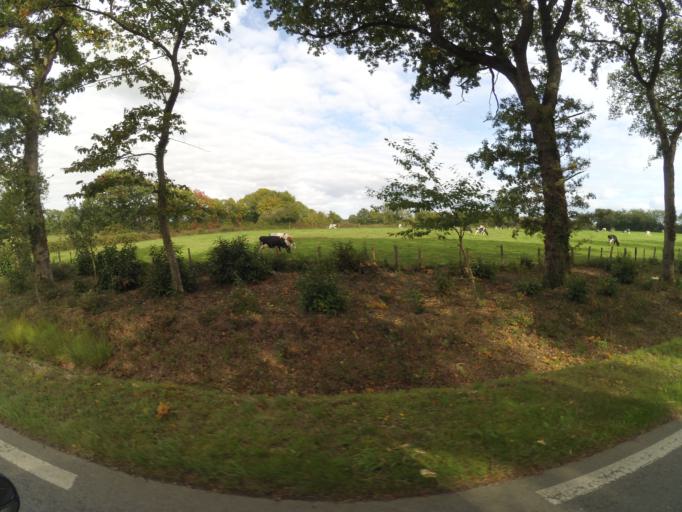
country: FR
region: Pays de la Loire
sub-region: Departement de la Loire-Atlantique
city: Plesse
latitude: 47.5268
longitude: -1.9006
